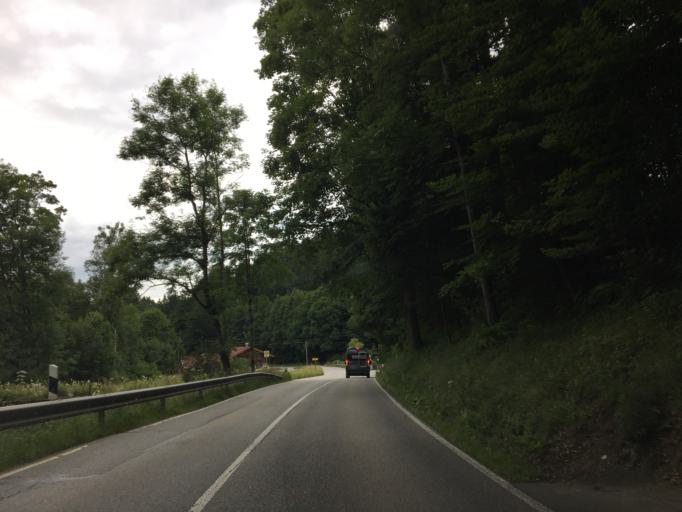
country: DE
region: Bavaria
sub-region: Upper Bavaria
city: Fischbachau
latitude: 47.7659
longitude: 11.9274
